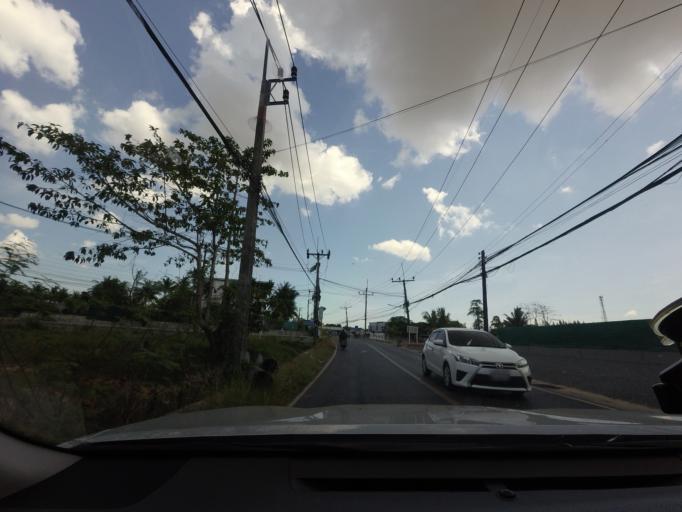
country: TH
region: Phuket
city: Thalang
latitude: 8.0175
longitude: 98.3153
